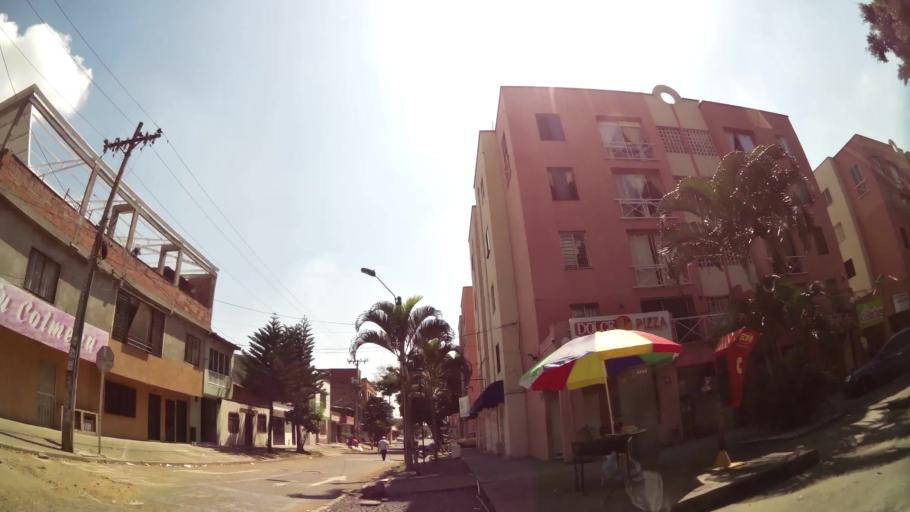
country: CO
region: Valle del Cauca
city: Cali
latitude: 3.4198
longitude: -76.5273
